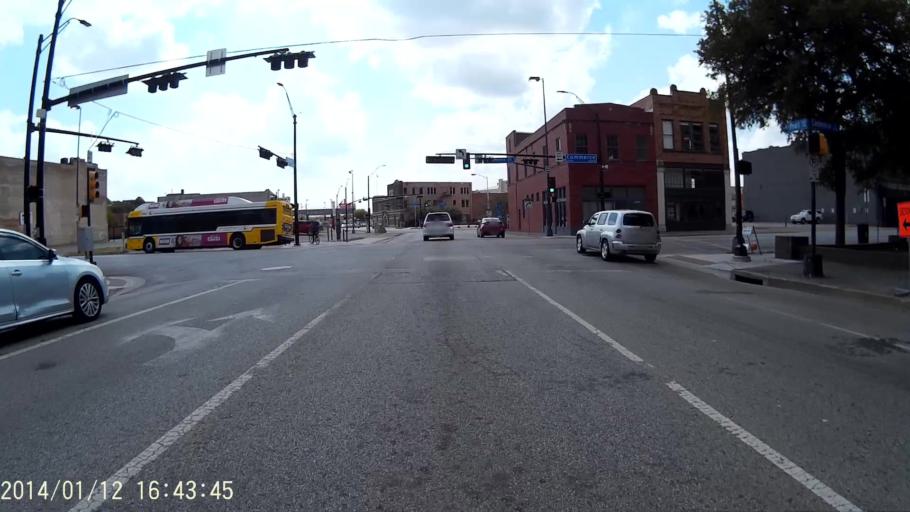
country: US
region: Texas
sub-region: Dallas County
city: Dallas
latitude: 32.7815
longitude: -96.7926
